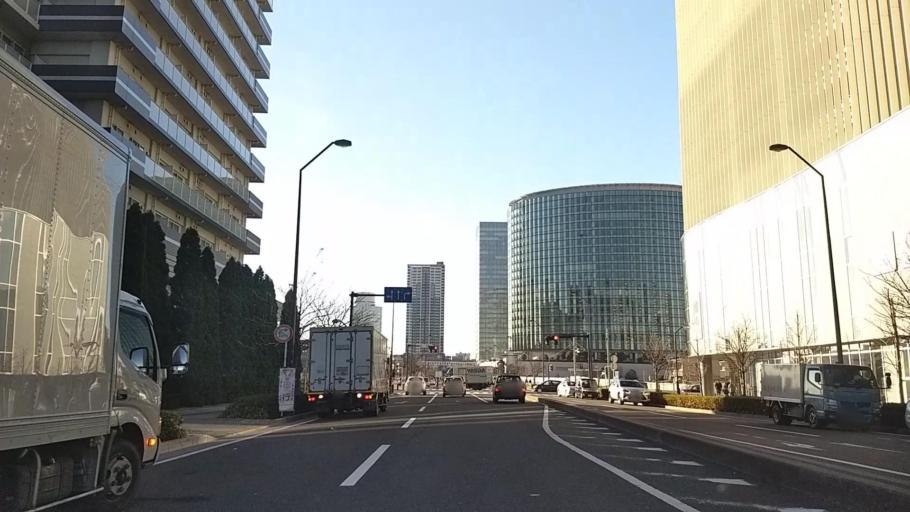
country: JP
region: Kanagawa
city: Yokohama
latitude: 35.4627
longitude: 139.6321
